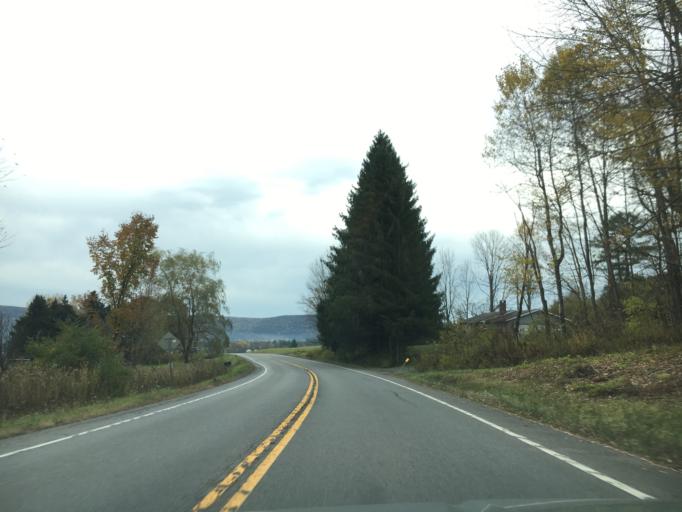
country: US
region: New York
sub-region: Otsego County
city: Cooperstown
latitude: 42.6054
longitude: -74.9555
